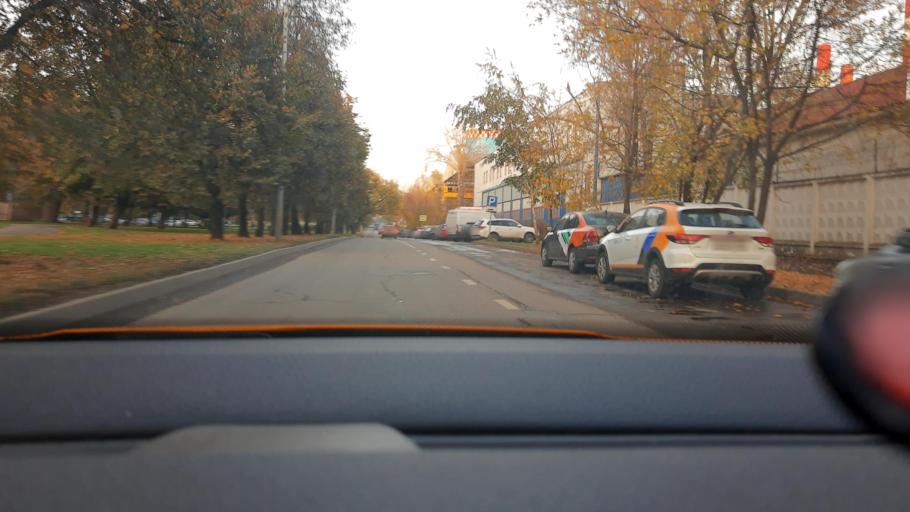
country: RU
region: Moscow
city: Metrogorodok
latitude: 55.8202
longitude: 37.7595
